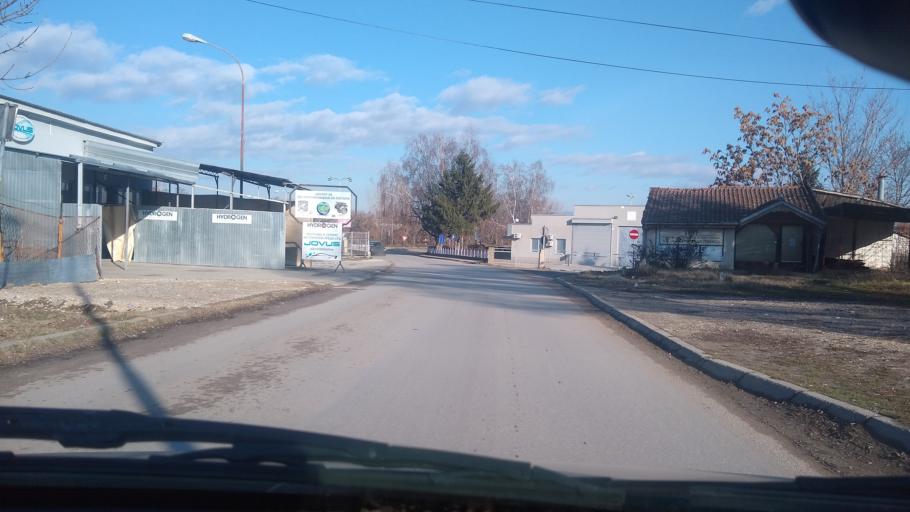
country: MK
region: Bitola
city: Bitola
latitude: 41.0125
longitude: 21.3474
